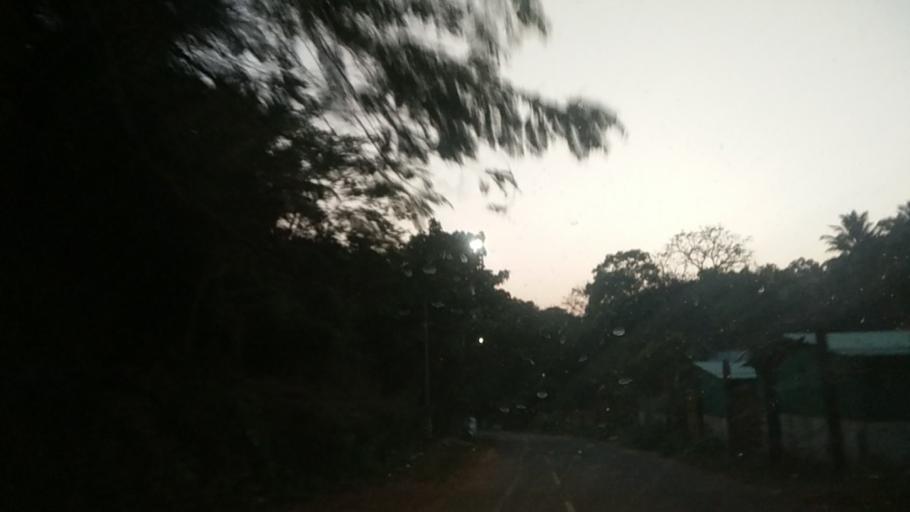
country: IN
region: Goa
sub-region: South Goa
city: Madgaon
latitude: 15.2768
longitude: 73.9689
